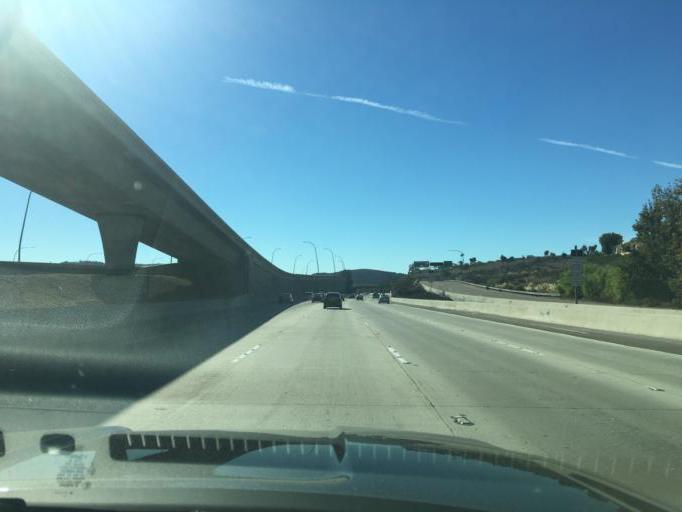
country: US
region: California
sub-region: San Diego County
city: Poway
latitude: 32.9624
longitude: -117.0972
